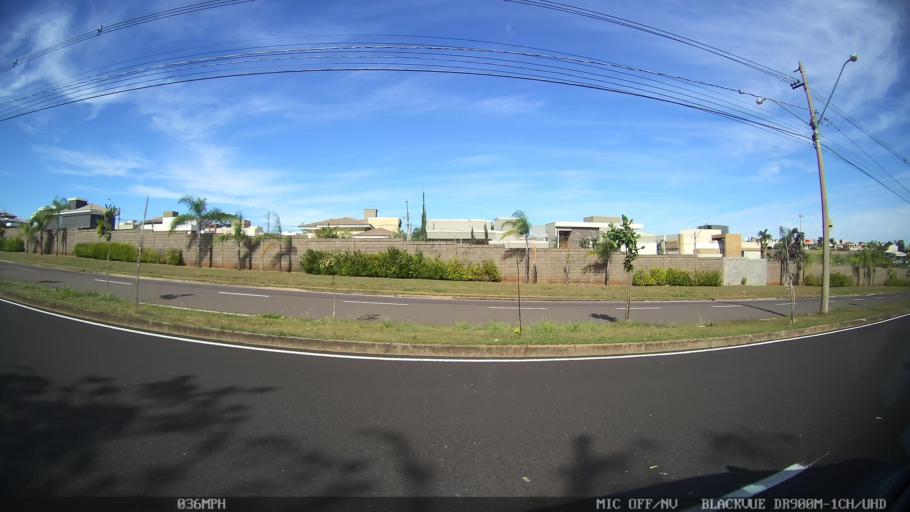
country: BR
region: Sao Paulo
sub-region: Sao Jose Do Rio Preto
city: Sao Jose do Rio Preto
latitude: -20.8106
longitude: -49.3354
